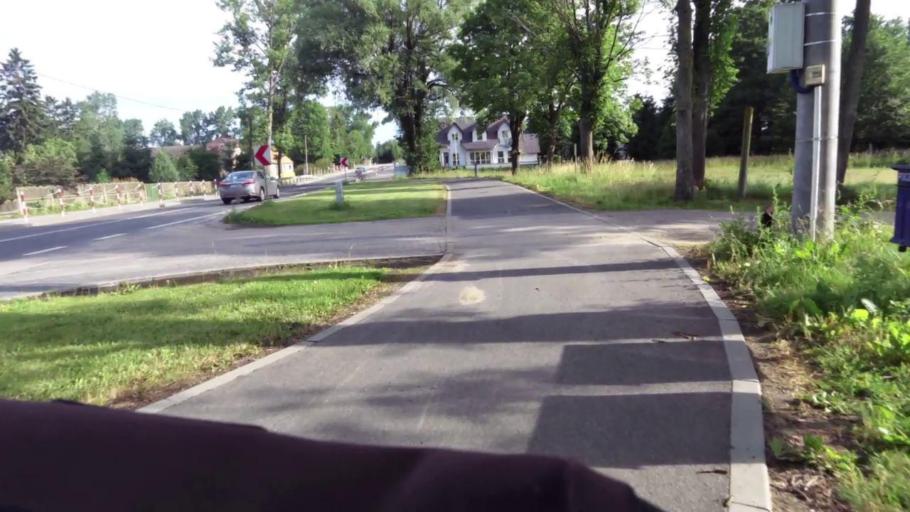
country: PL
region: West Pomeranian Voivodeship
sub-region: Powiat kamienski
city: Kamien Pomorski
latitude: 53.9972
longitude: 14.8174
